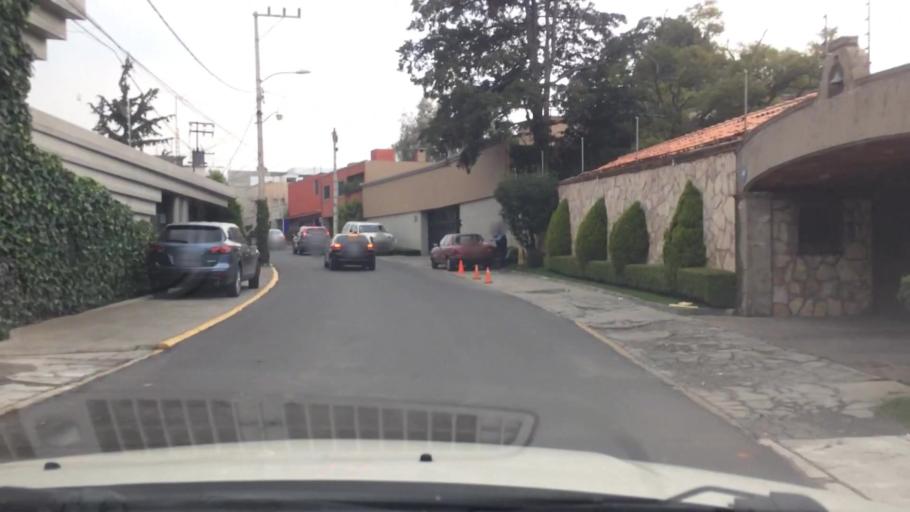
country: MX
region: Mexico City
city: Magdalena Contreras
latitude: 19.3154
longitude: -99.2098
